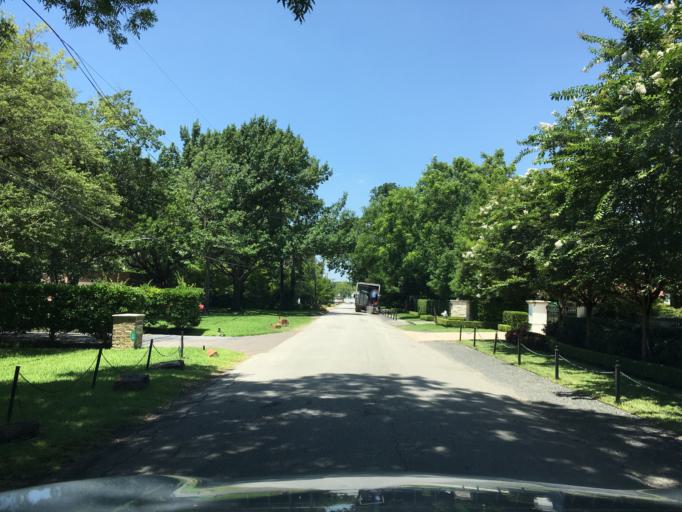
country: US
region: Texas
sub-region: Dallas County
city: University Park
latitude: 32.8750
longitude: -96.8049
